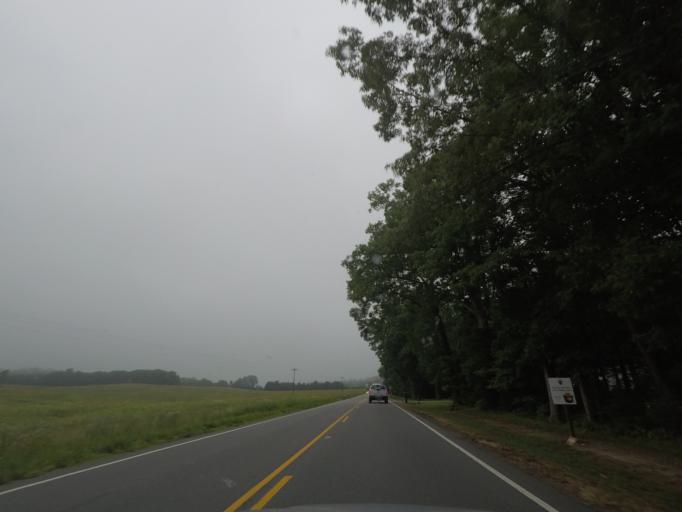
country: US
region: Virginia
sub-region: Prince Edward County
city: Farmville
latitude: 37.3612
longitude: -78.4841
